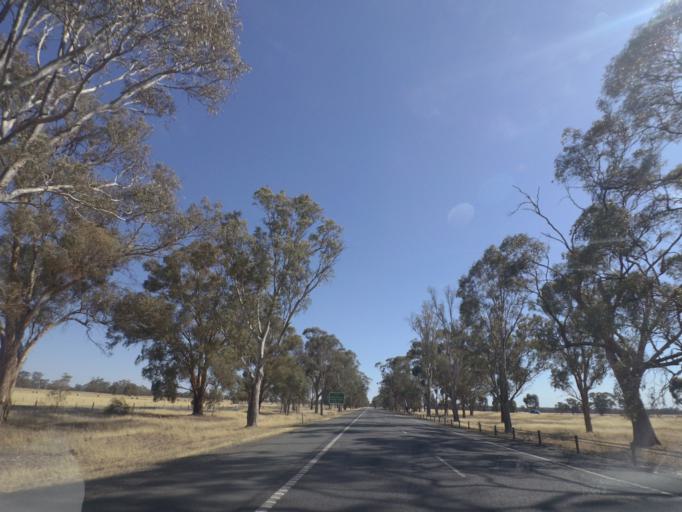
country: AU
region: Victoria
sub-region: Greater Shepparton
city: Shepparton
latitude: -36.6026
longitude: 145.3249
